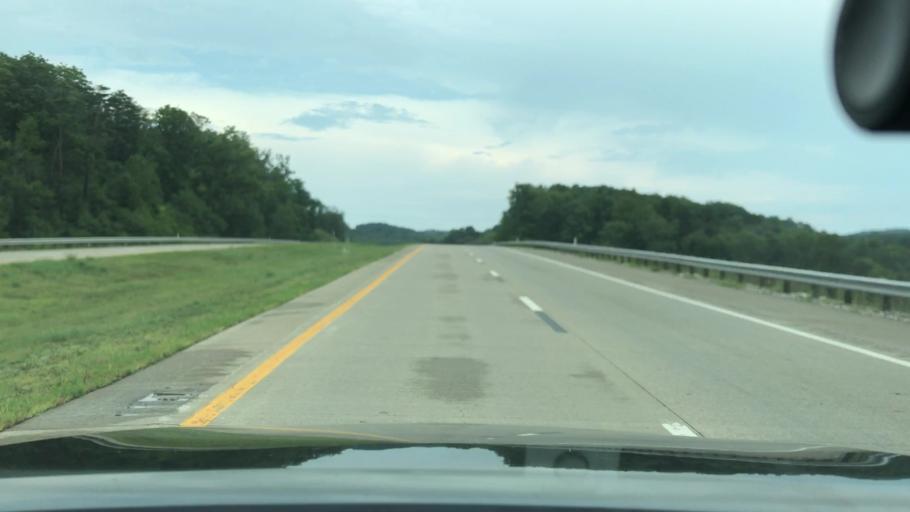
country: US
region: West Virginia
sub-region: Mason County
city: Point Pleasant
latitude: 38.7749
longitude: -82.0579
